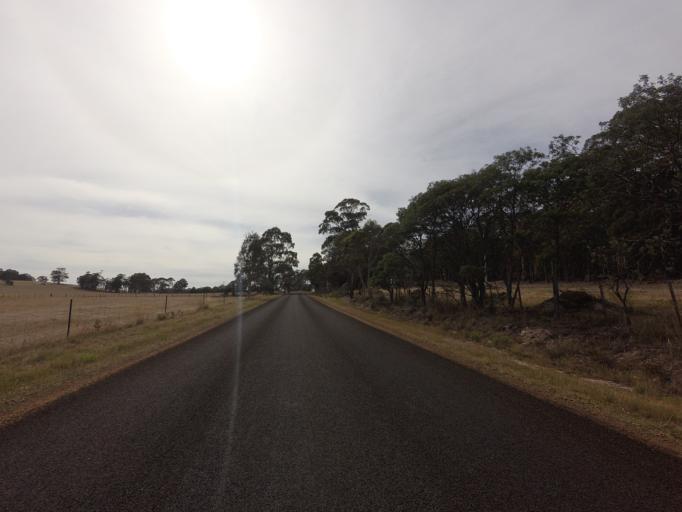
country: AU
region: Tasmania
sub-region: Sorell
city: Sorell
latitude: -42.4260
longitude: 147.4852
